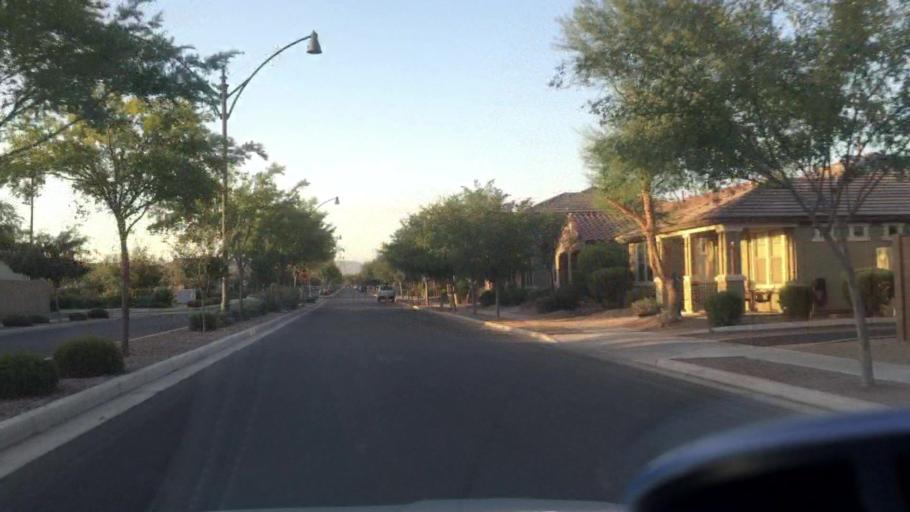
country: US
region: Arizona
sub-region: Maricopa County
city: Gilbert
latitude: 33.3154
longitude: -111.7169
